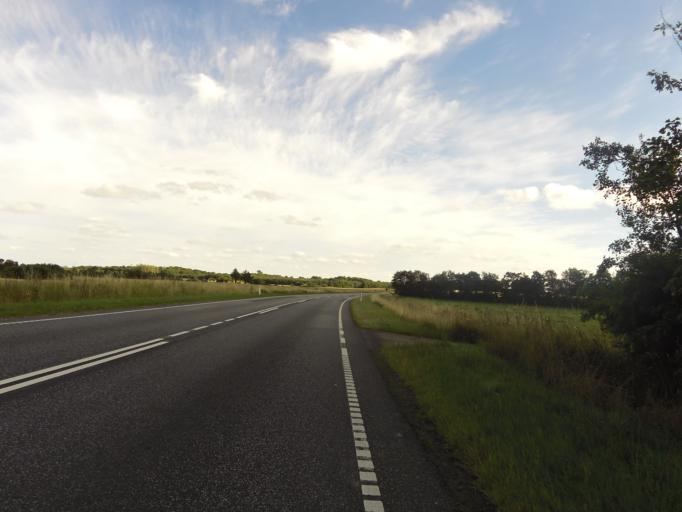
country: DK
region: South Denmark
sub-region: Tonder Kommune
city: Toftlund
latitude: 55.2062
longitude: 9.0479
